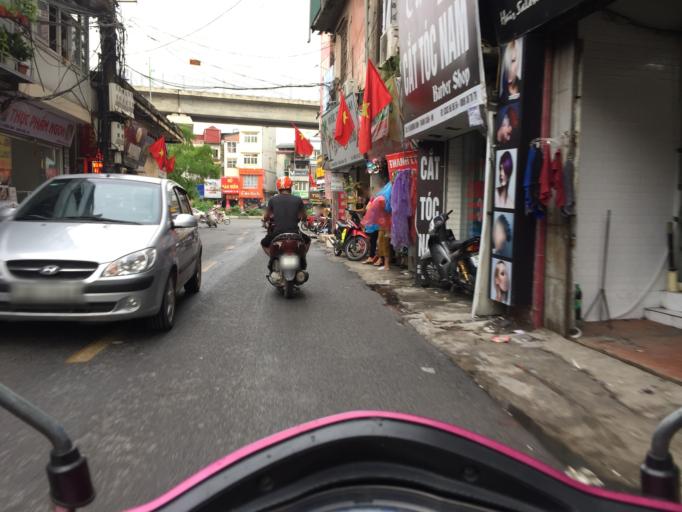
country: VN
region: Ha Noi
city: Thanh Xuan
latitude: 20.9977
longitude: 105.8135
